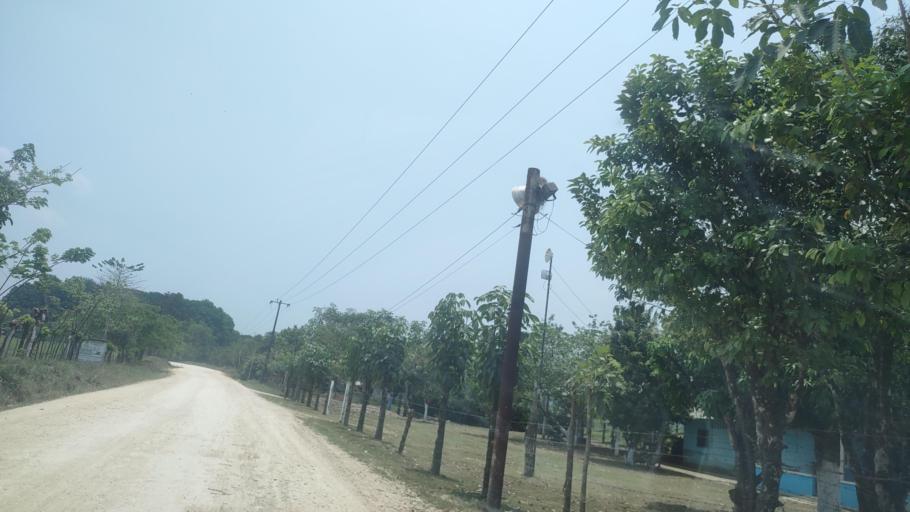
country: MX
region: Chiapas
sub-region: Tecpatan
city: Raudales Malpaso
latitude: 17.4607
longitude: -93.8056
